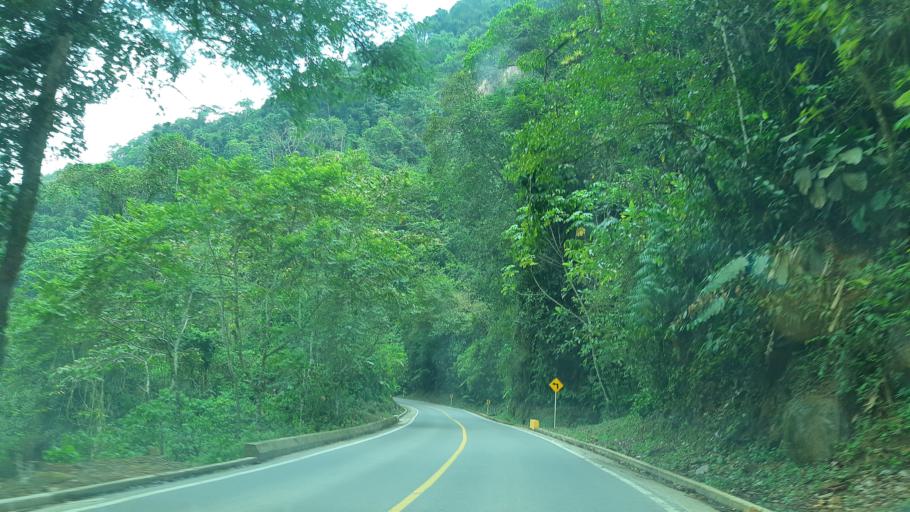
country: CO
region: Boyaca
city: Santa Maria
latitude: 4.8482
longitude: -73.2270
